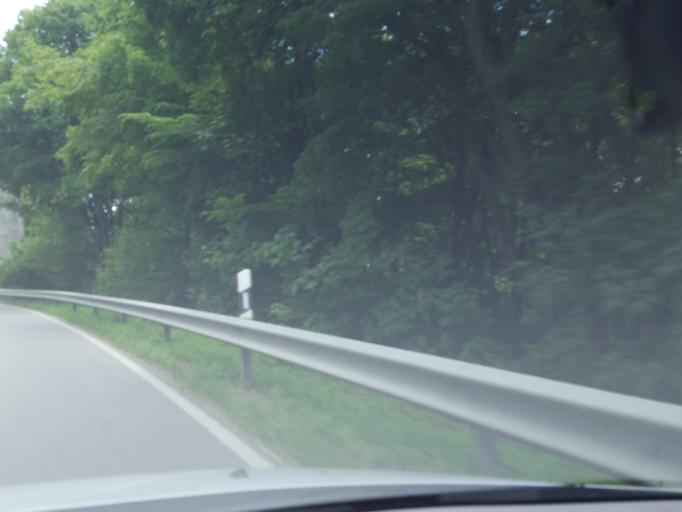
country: DE
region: Bavaria
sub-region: Lower Bavaria
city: Vilsbiburg
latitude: 48.4405
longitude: 12.3520
